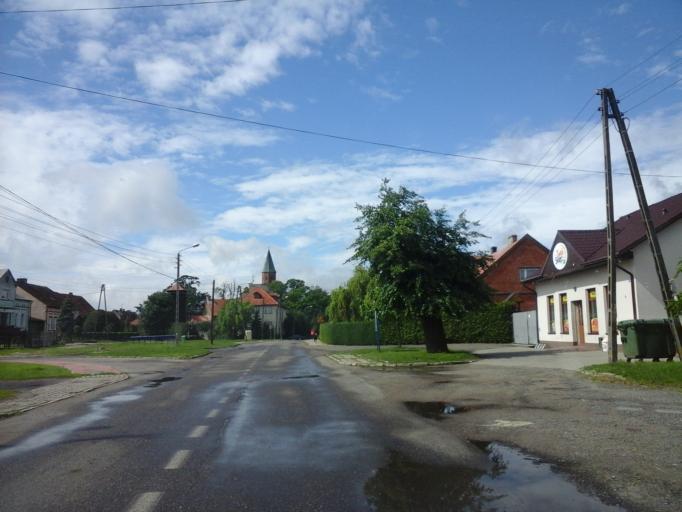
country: PL
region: West Pomeranian Voivodeship
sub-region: Powiat choszczenski
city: Krzecin
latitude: 53.0688
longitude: 15.4338
